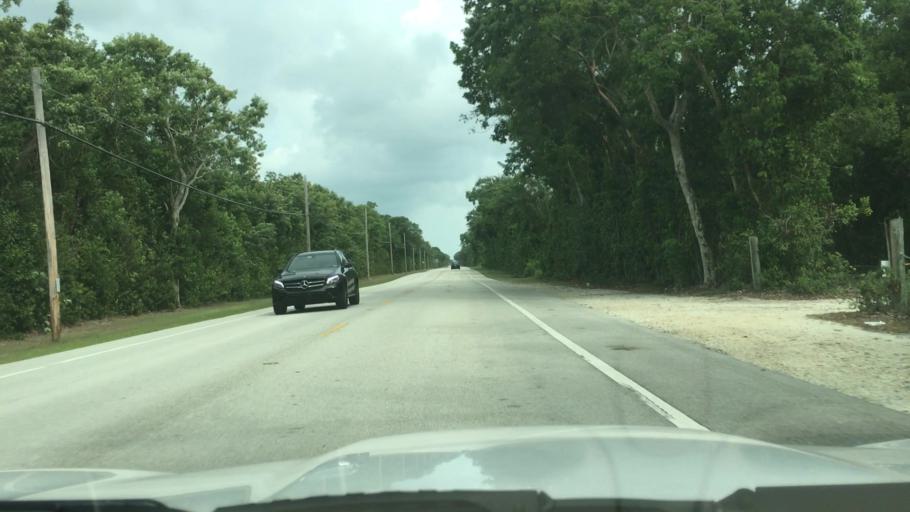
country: US
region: Florida
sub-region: Monroe County
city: North Key Largo
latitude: 25.1847
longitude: -80.3623
